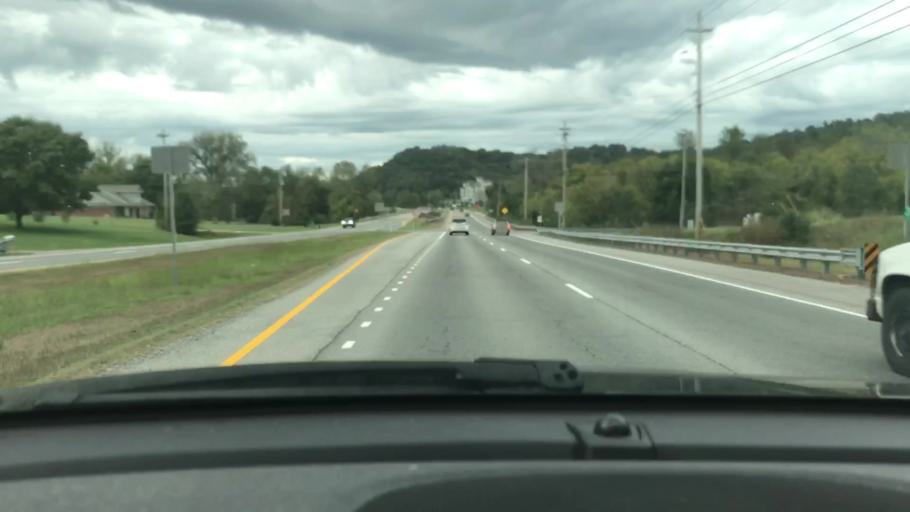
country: US
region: Tennessee
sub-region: Cheatham County
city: Ashland City
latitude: 36.2395
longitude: -87.0221
